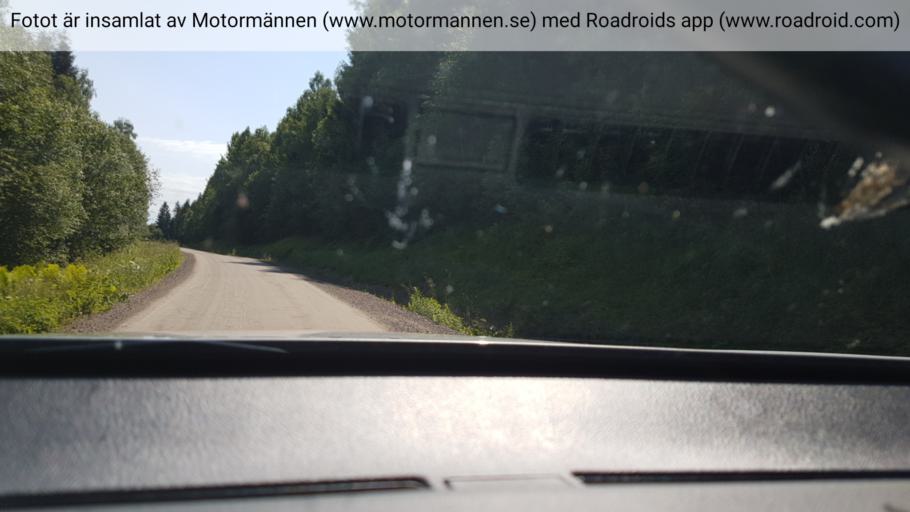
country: SE
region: Vaermland
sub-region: Torsby Kommun
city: Torsby
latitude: 60.5154
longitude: 13.1308
